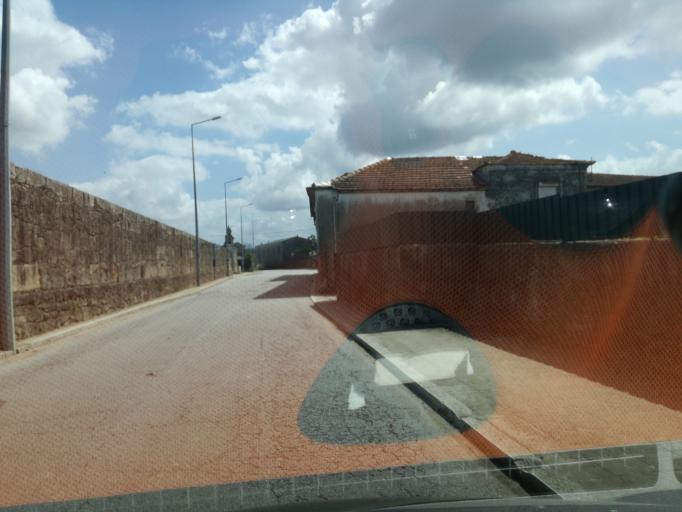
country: PT
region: Porto
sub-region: Valongo
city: Ermesinde
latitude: 41.2282
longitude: -8.5636
